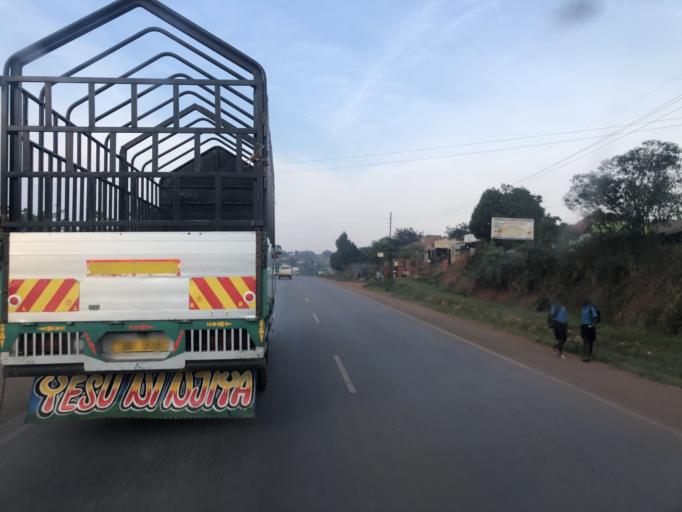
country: UG
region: Central Region
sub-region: Mpigi District
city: Mpigi
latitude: 0.2491
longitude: 32.3879
